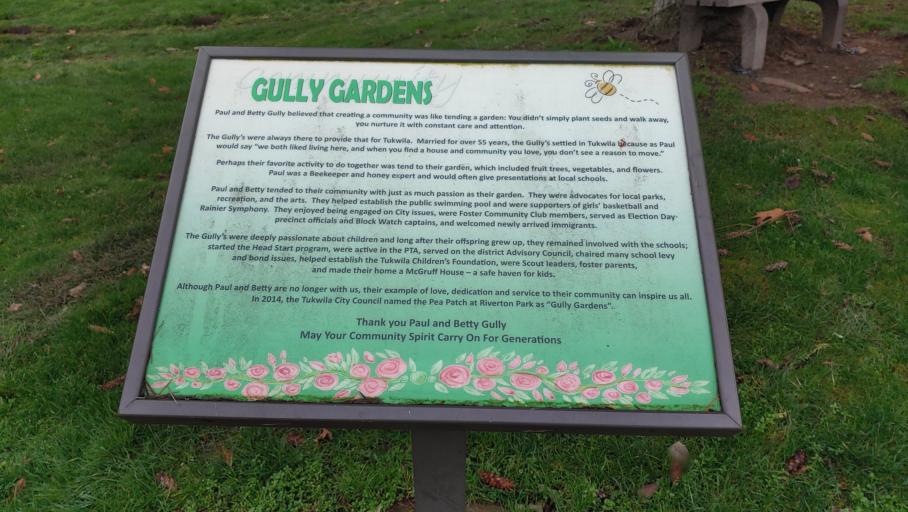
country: US
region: Washington
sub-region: King County
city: Riverton
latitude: 47.4853
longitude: -122.2812
